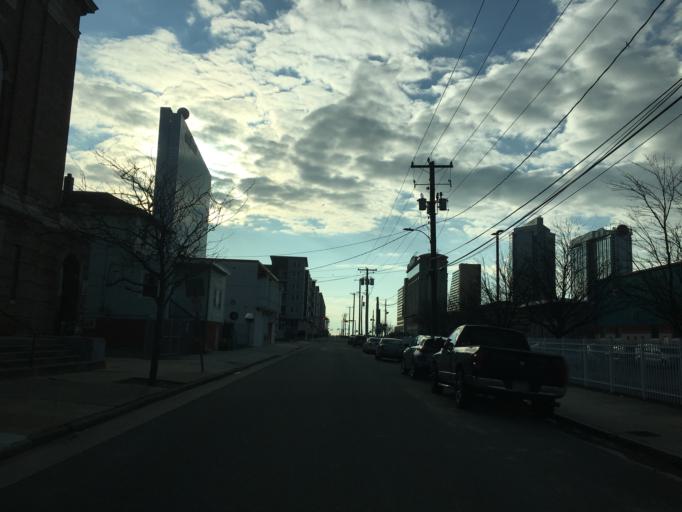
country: US
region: New Jersey
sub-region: Atlantic County
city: Atlantic City
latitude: 39.3668
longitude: -74.4201
